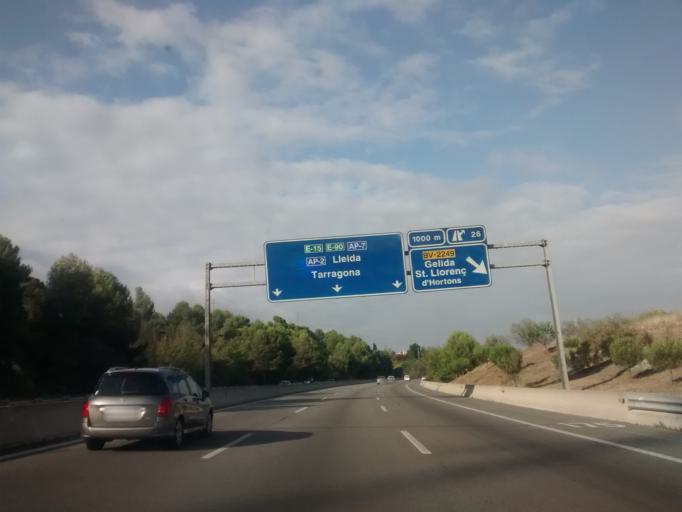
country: ES
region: Catalonia
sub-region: Provincia de Barcelona
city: Gelida
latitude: 41.4483
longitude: 1.8756
